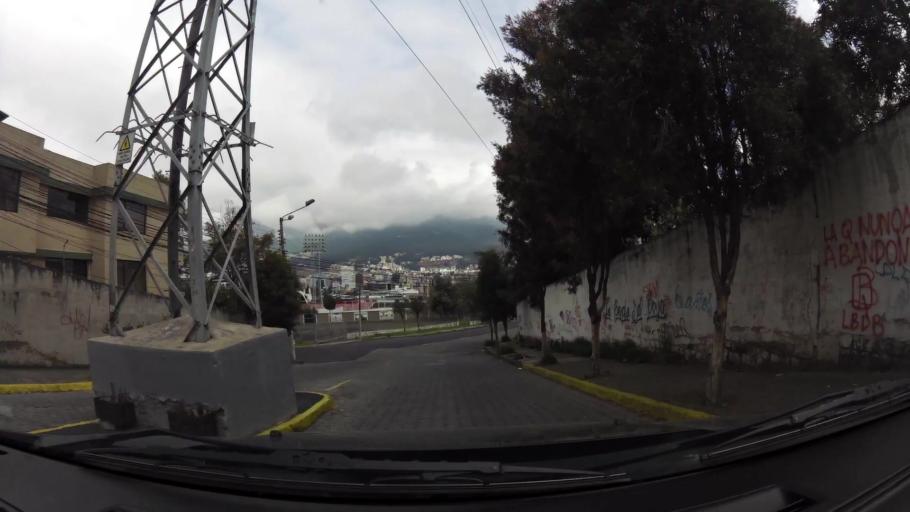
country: EC
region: Pichincha
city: Quito
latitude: -0.1770
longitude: -78.4743
